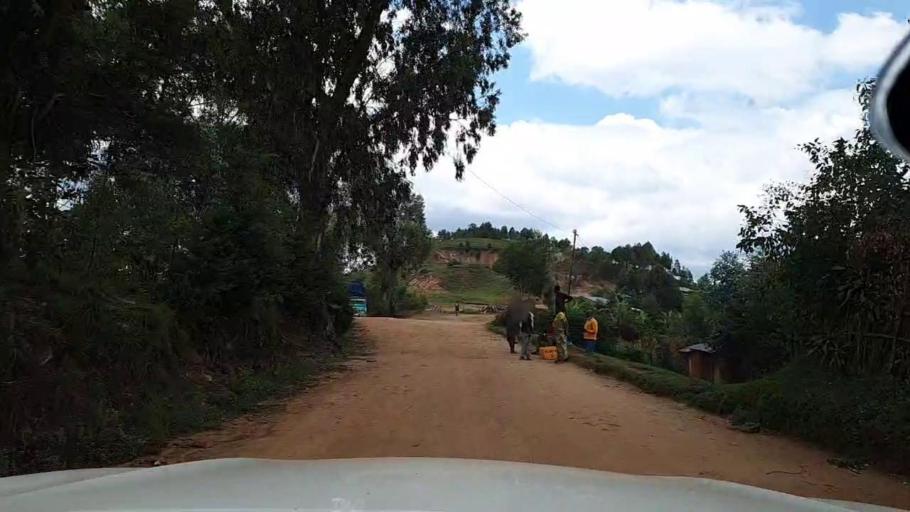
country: RW
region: Southern Province
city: Nzega
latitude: -2.7081
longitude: 29.5146
